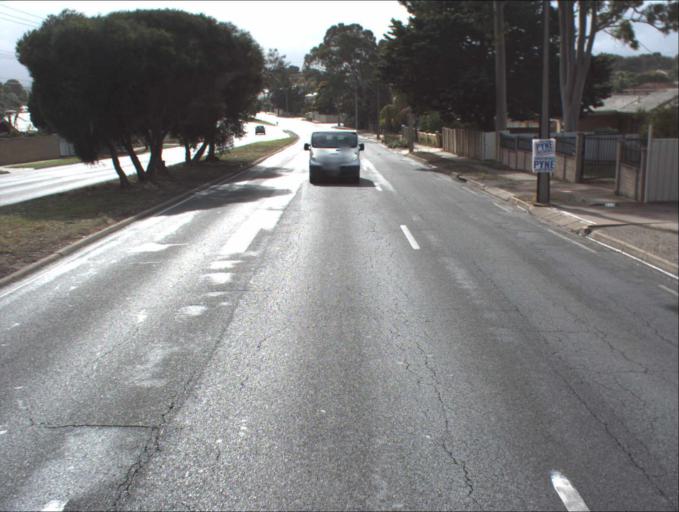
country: AU
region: South Australia
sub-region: Port Adelaide Enfield
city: Gilles Plains
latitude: -34.8509
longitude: 138.6678
